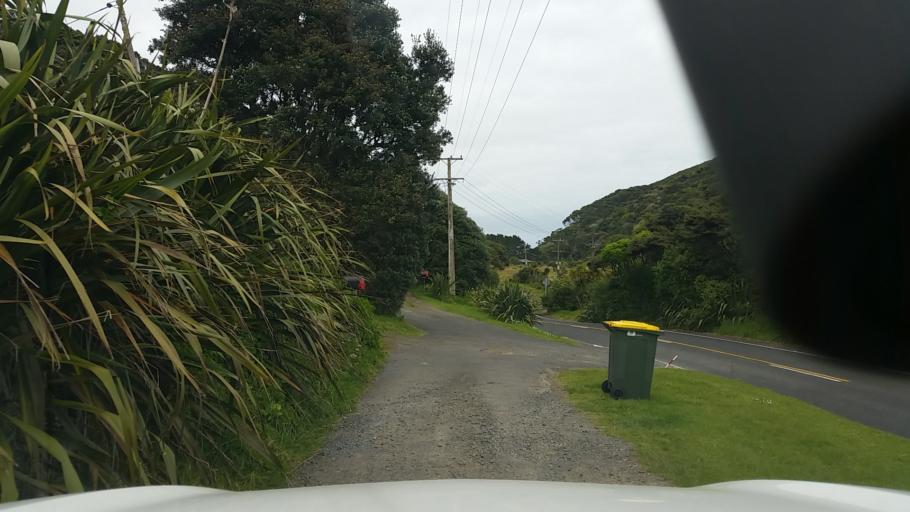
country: NZ
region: Auckland
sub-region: Auckland
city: Muriwai Beach
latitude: -36.8808
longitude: 174.4514
